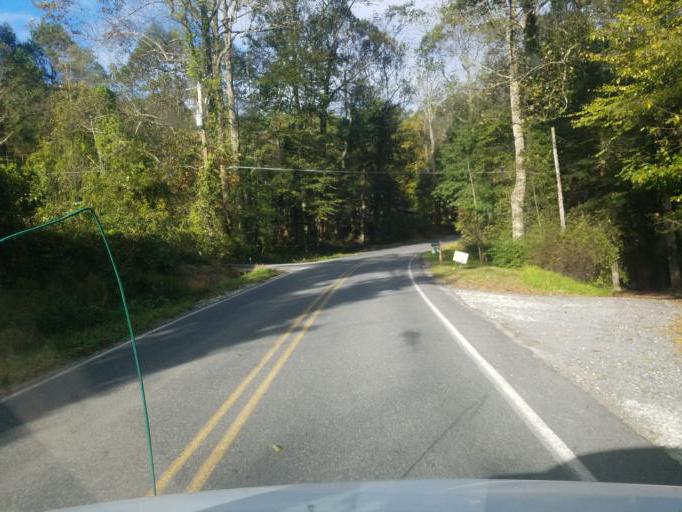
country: US
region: Pennsylvania
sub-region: Franklin County
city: Fayetteville
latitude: 39.8954
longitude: -77.4081
